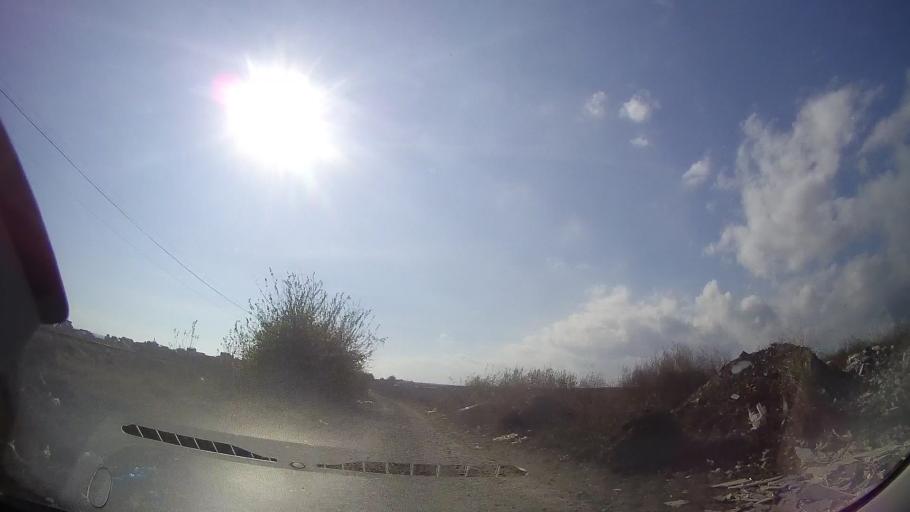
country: RO
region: Constanta
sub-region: Comuna Costinesti
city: Costinesti
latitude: 43.9674
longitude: 28.6410
